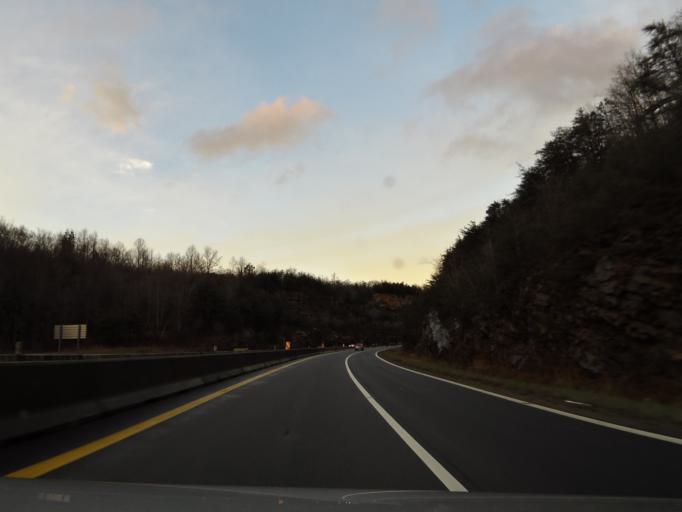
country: US
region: Tennessee
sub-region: Campbell County
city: Jacksboro
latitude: 36.4329
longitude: -84.2934
